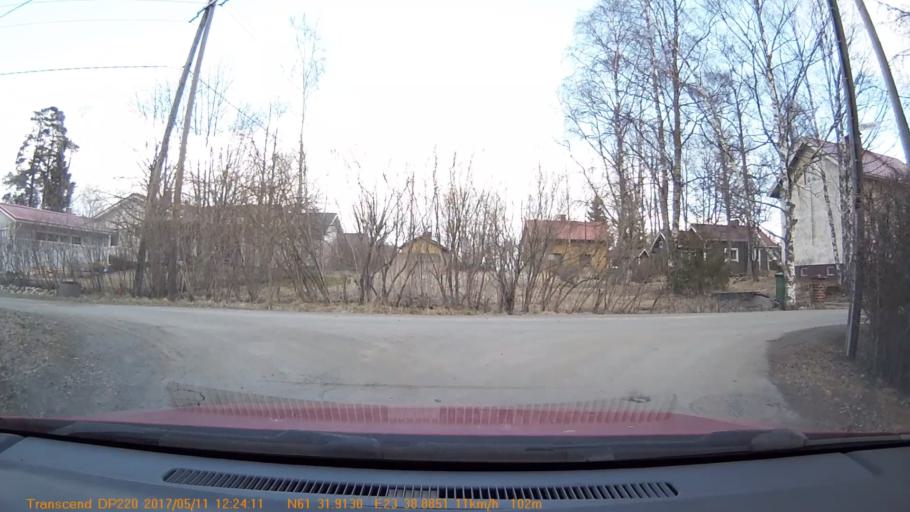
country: FI
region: Pirkanmaa
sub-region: Tampere
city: Yloejaervi
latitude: 61.5319
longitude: 23.6480
